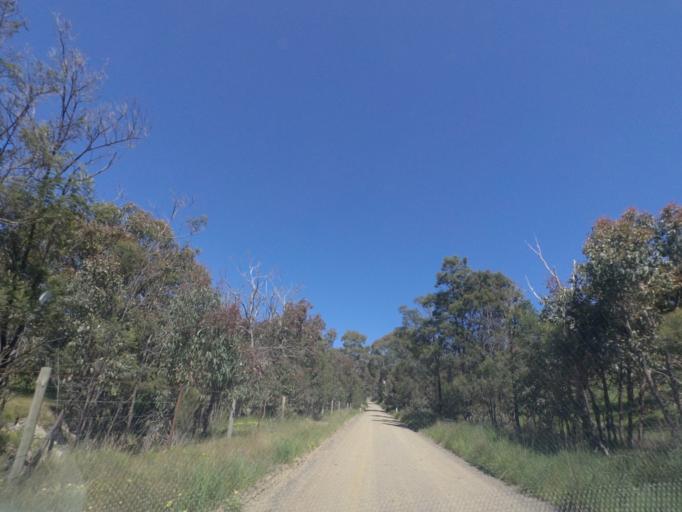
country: AU
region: Victoria
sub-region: Whittlesea
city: Whittlesea
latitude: -37.2794
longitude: 145.0143
